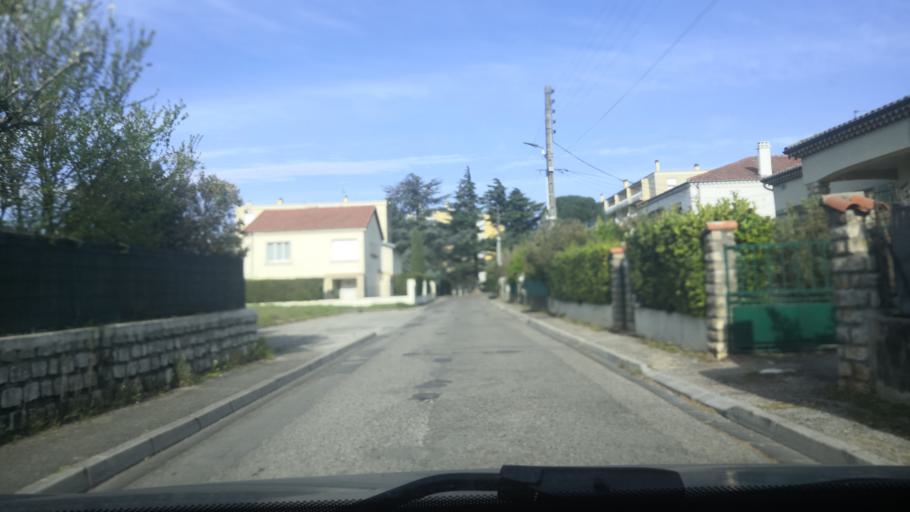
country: FR
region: Rhone-Alpes
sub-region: Departement de la Drome
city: Montelimar
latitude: 44.5454
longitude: 4.7439
